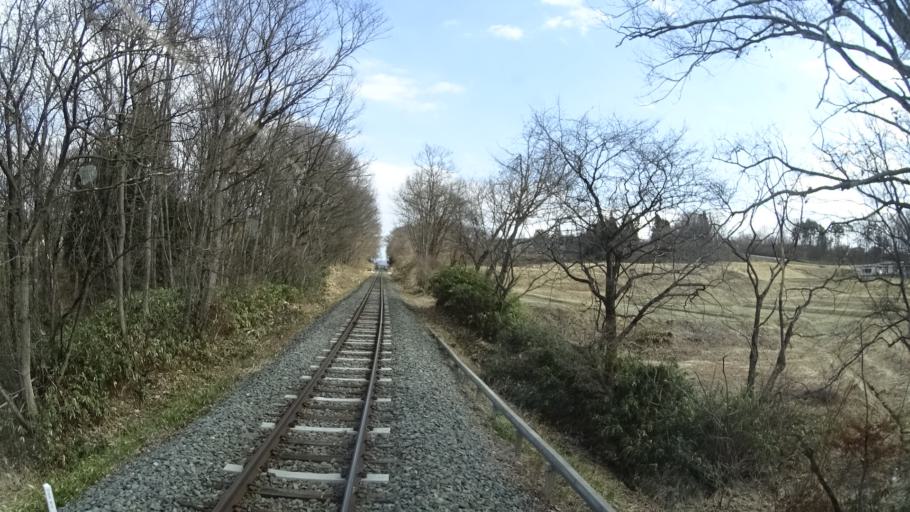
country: JP
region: Iwate
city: Hanamaki
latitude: 39.3929
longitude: 141.2149
